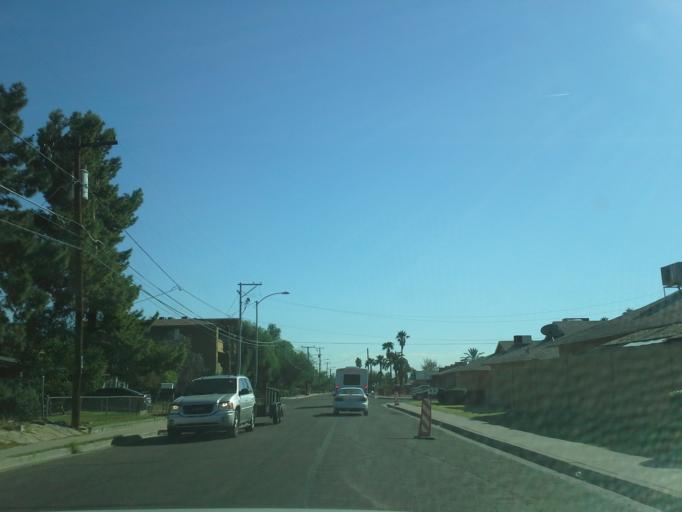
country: US
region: Arizona
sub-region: Maricopa County
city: Glendale
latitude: 33.5756
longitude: -112.0848
